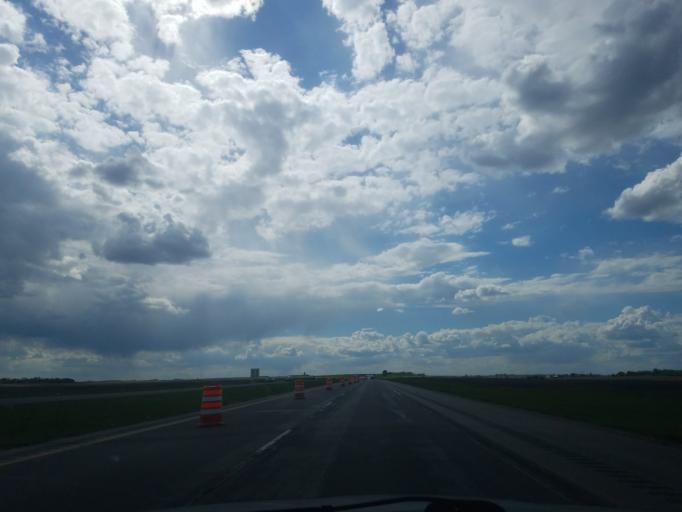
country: US
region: North Dakota
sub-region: Barnes County
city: Valley City
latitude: 46.9201
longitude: -97.7723
